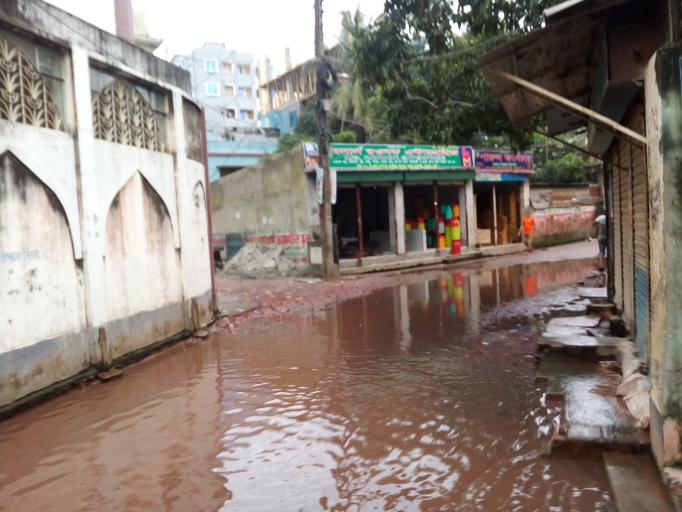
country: BD
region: Dhaka
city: Tungi
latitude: 23.8424
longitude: 90.2540
